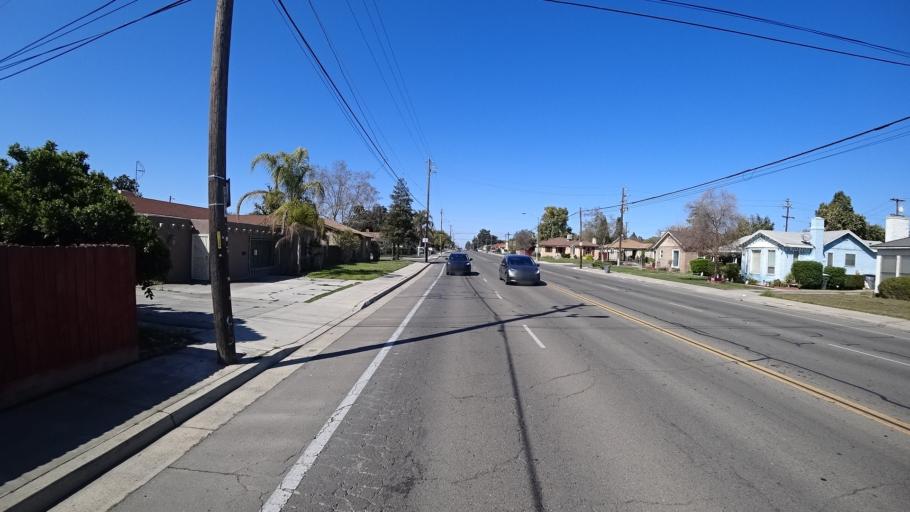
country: US
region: California
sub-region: Fresno County
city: Fresno
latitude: 36.7649
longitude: -119.8103
